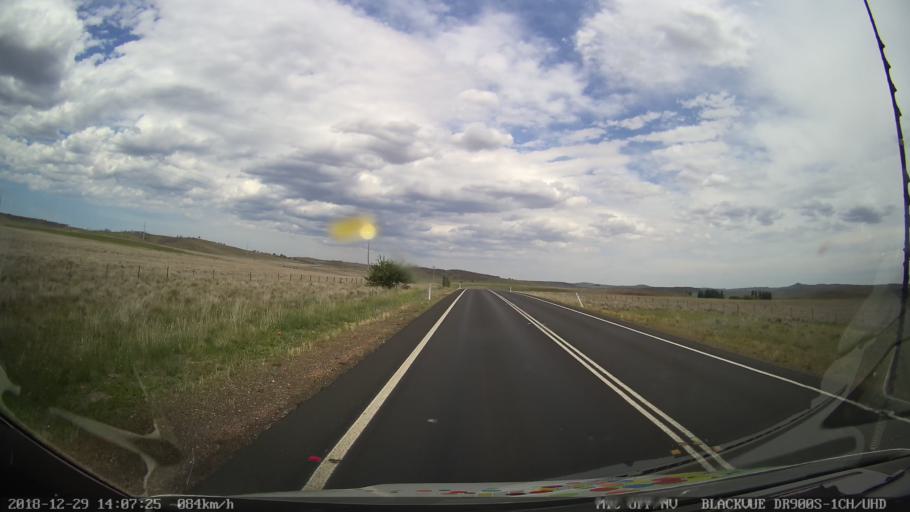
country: AU
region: New South Wales
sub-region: Cooma-Monaro
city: Cooma
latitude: -36.3515
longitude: 149.2136
